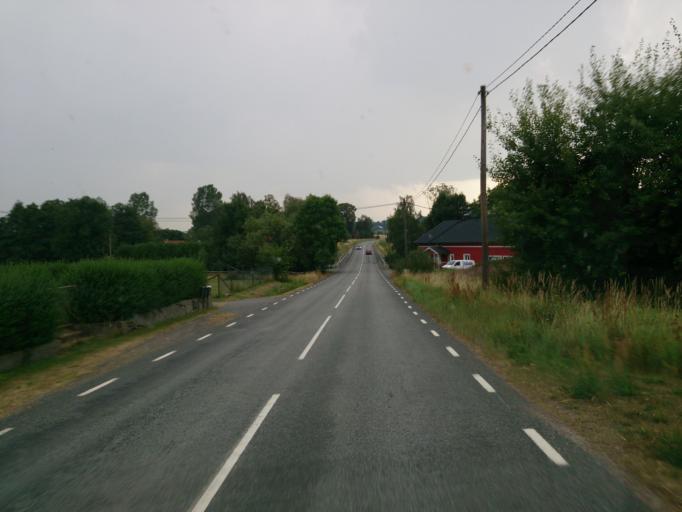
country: SE
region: Skane
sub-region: Ostra Goinge Kommun
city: Sibbhult
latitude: 56.2060
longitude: 14.1616
